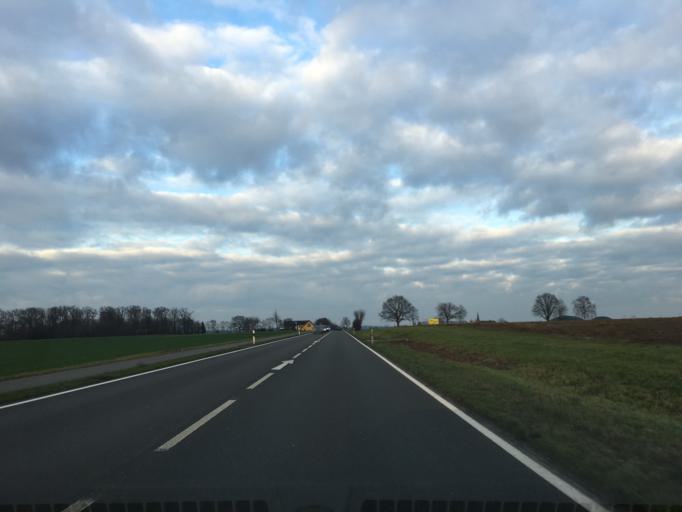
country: DE
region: North Rhine-Westphalia
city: Olfen
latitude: 51.6937
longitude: 7.3640
